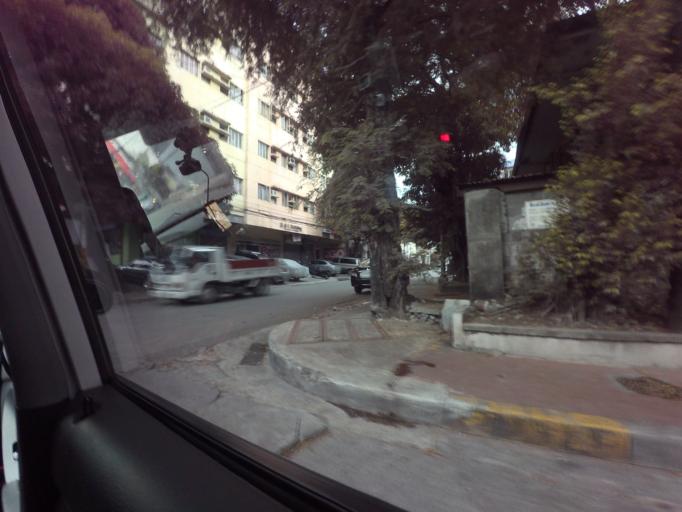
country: PH
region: Metro Manila
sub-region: City of Manila
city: Manila
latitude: 14.6170
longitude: 121.0044
